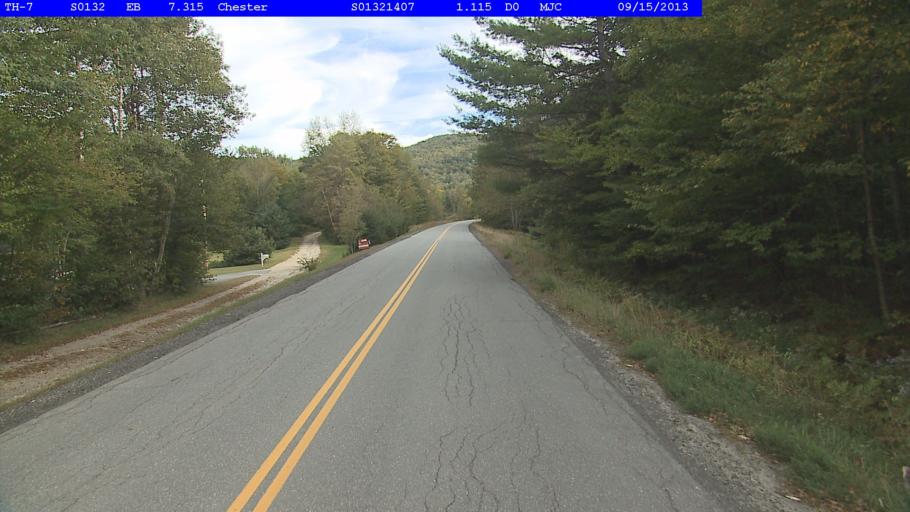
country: US
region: Vermont
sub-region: Windsor County
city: Chester
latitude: 43.2667
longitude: -72.6650
